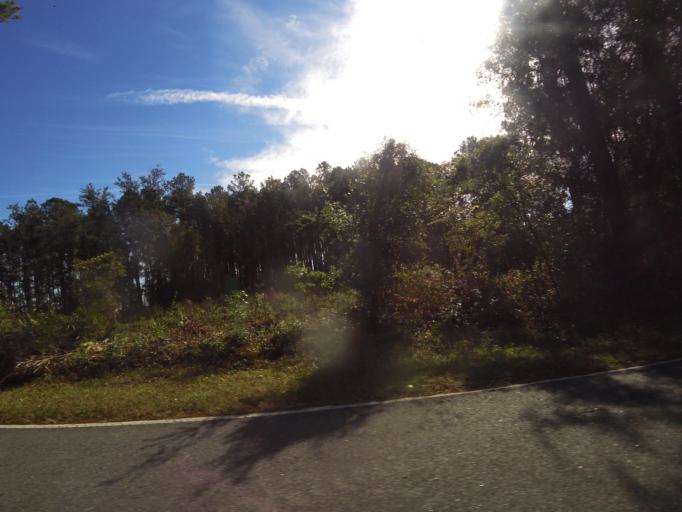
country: US
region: Georgia
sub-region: Glynn County
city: Brunswick
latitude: 31.1349
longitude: -81.5613
